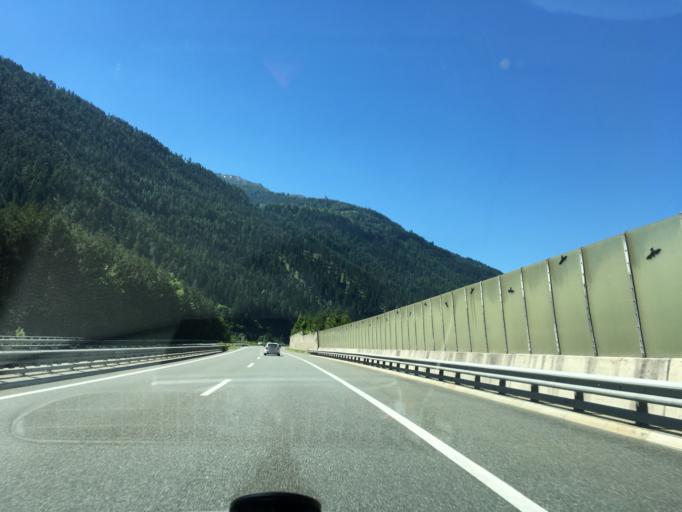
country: AT
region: Tyrol
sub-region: Politischer Bezirk Landeck
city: Schonwies
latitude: 47.1940
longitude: 10.6458
